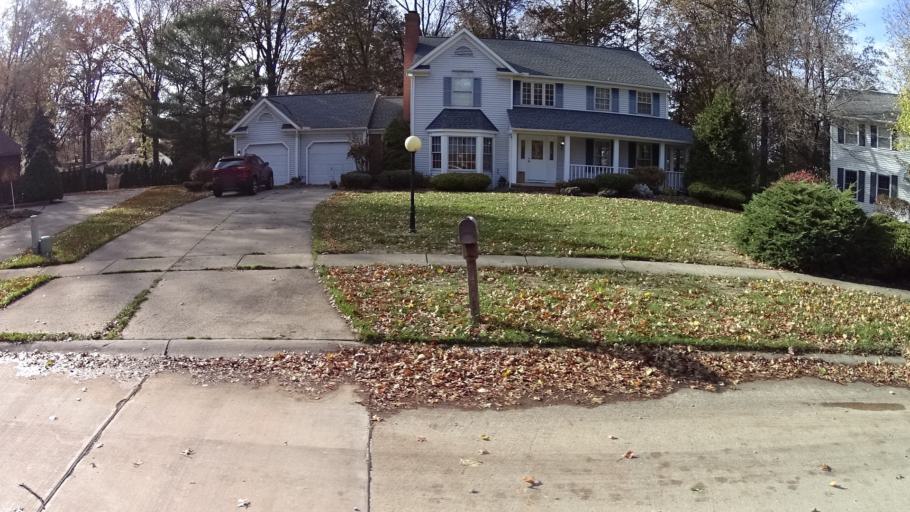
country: US
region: Ohio
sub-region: Lorain County
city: Avon Lake
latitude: 41.5064
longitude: -81.9811
